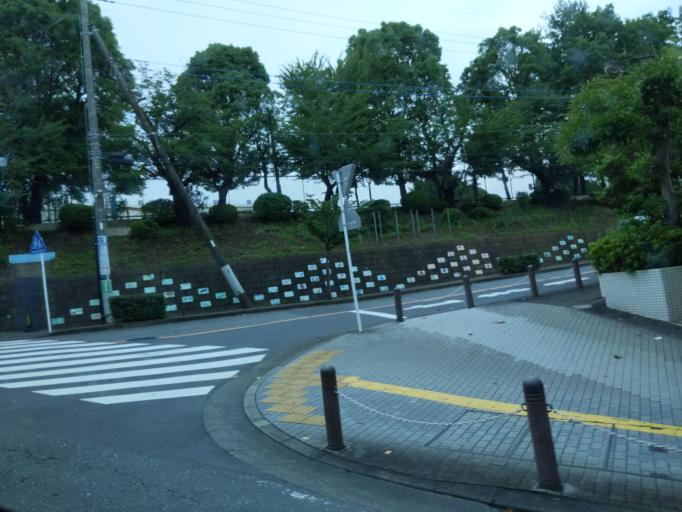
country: JP
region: Tokyo
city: Chofugaoka
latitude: 35.5872
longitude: 139.5797
